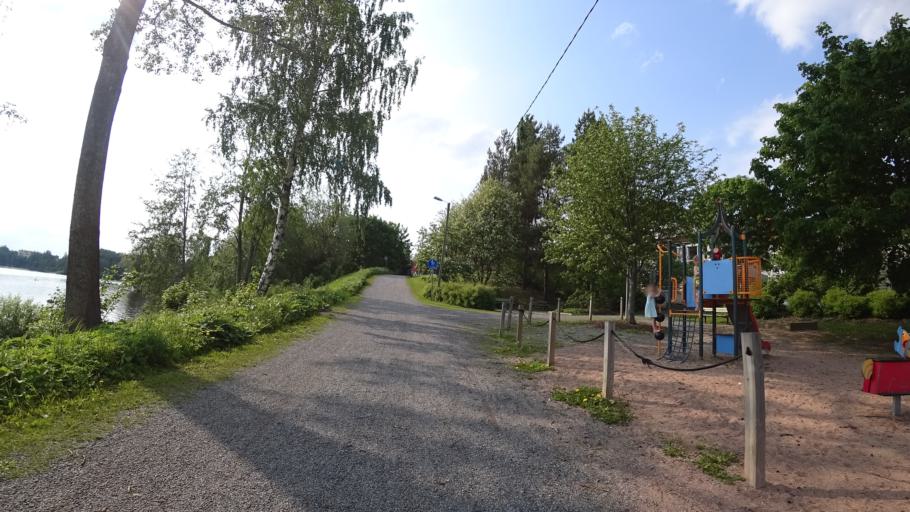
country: FI
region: Pirkanmaa
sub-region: Tampere
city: Pirkkala
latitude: 61.5032
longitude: 23.7026
